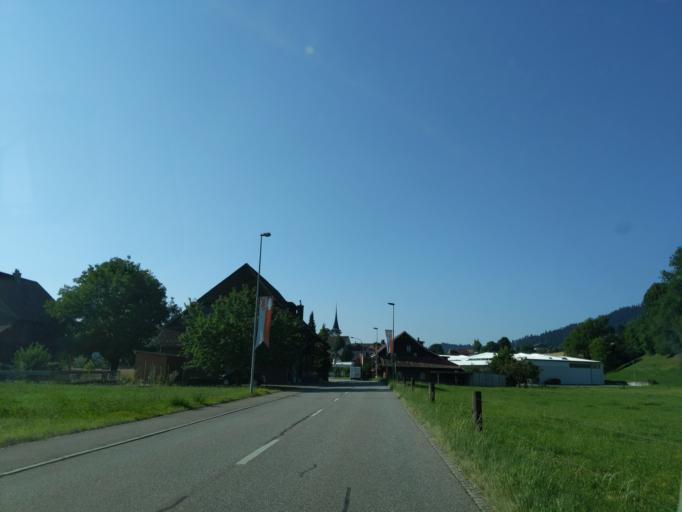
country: CH
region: Bern
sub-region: Emmental District
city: Lauperswil
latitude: 46.9701
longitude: 7.7404
